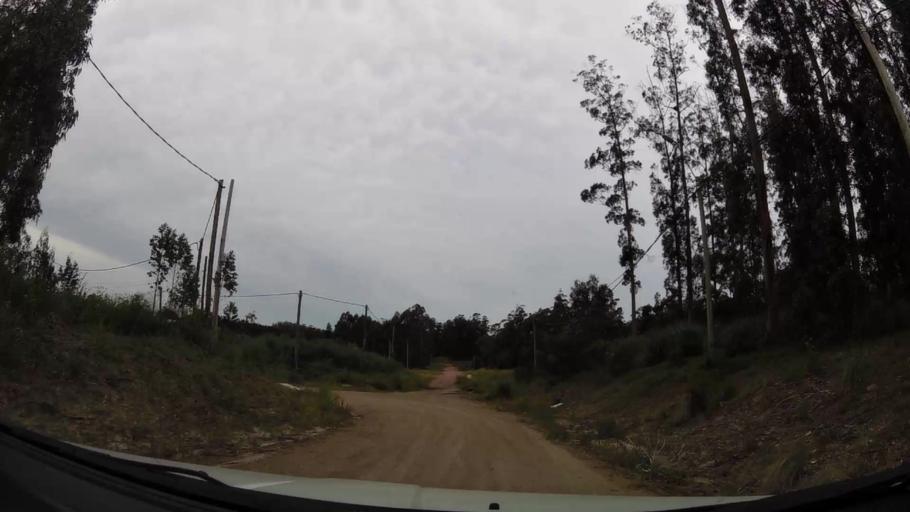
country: UY
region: Maldonado
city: Maldonado
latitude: -34.8989
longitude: -54.9894
